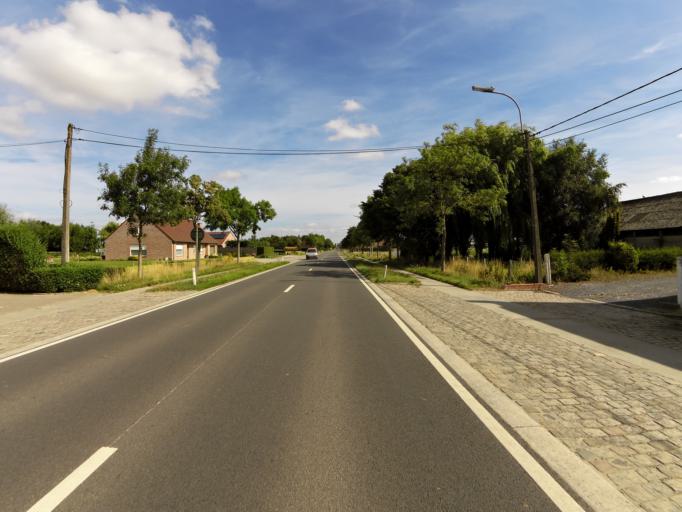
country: BE
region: Flanders
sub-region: Provincie West-Vlaanderen
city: Diksmuide
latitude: 50.9498
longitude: 2.8631
